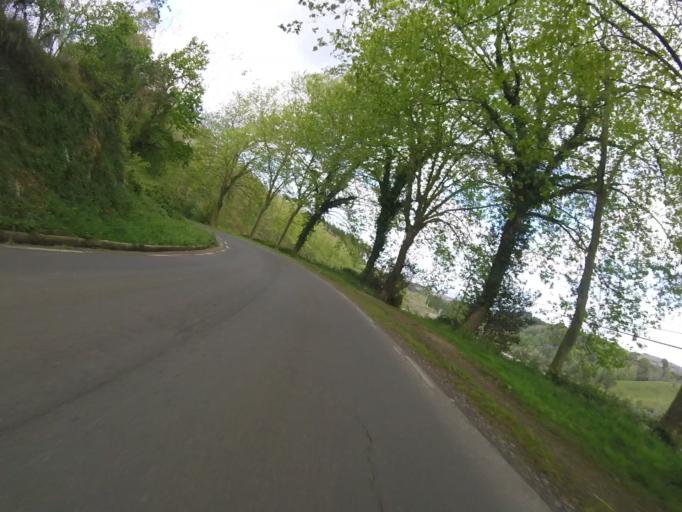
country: ES
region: Basque Country
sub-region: Provincia de Guipuzcoa
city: Zarautz
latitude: 43.2665
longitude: -2.1660
